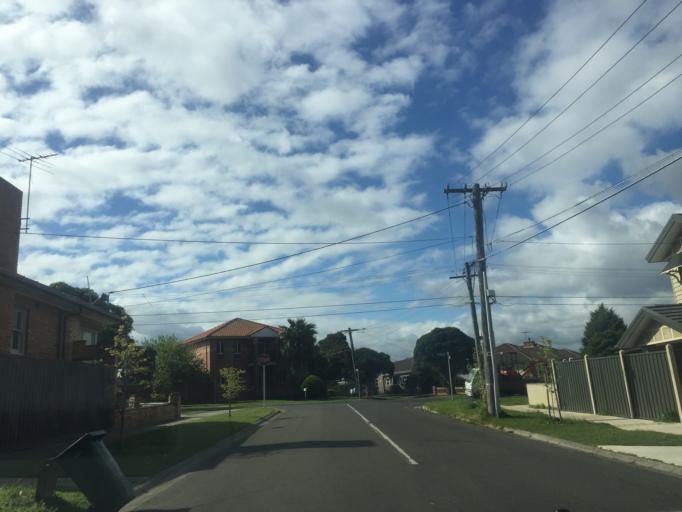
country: AU
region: Victoria
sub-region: Darebin
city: Kingsbury
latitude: -37.7255
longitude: 145.0206
